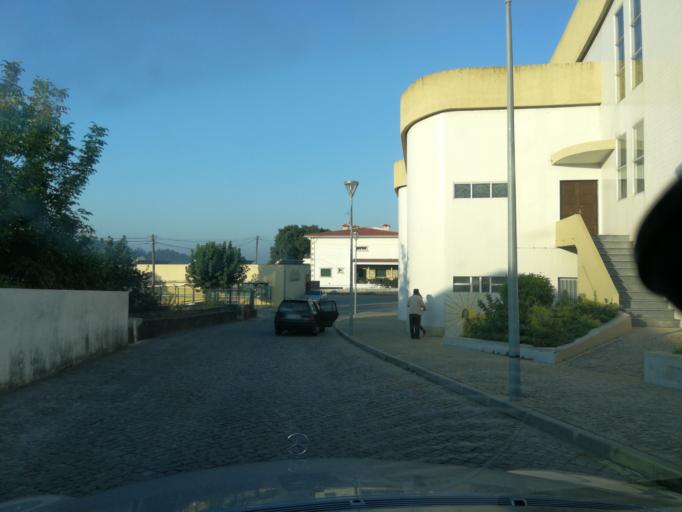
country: PT
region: Braga
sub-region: Braga
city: Braga
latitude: 41.5299
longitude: -8.4274
